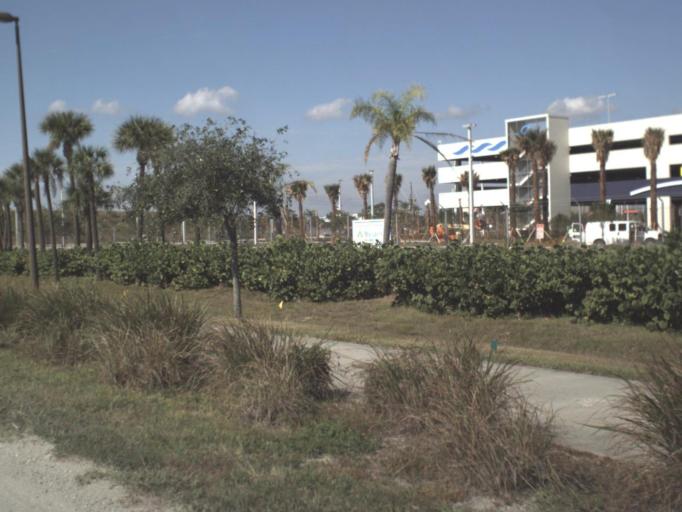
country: US
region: Florida
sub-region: Brevard County
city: Cape Canaveral
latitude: 28.4051
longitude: -80.6119
